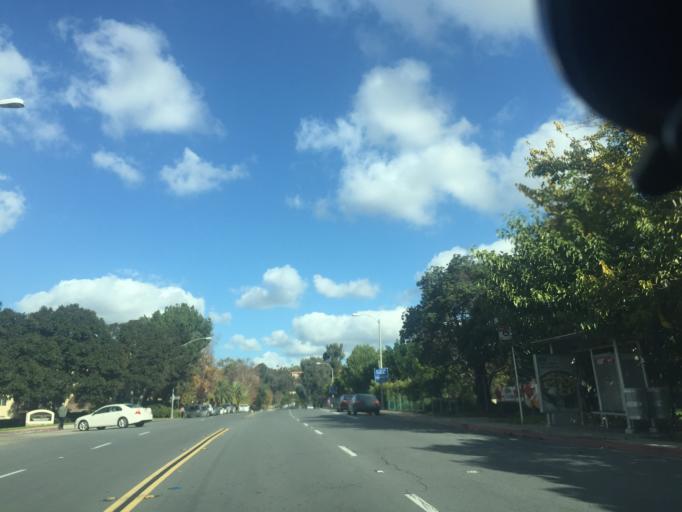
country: US
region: California
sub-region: San Diego County
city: San Diego
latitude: 32.7813
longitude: -117.1104
